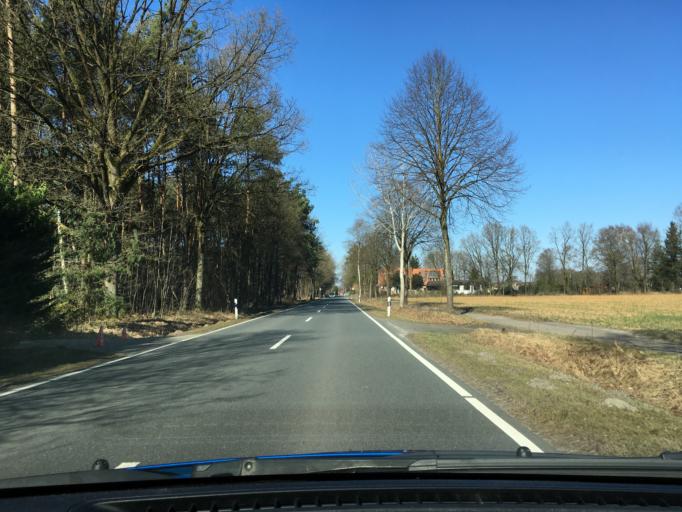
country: DE
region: Lower Saxony
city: Schneverdingen
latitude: 53.0799
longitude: 9.8096
